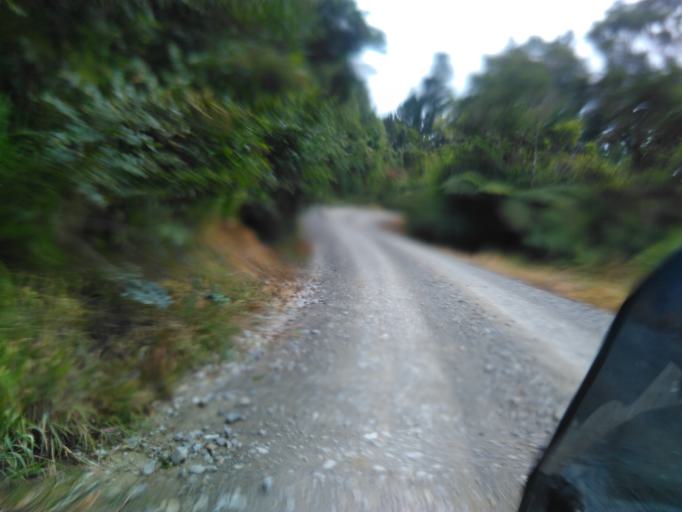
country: NZ
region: Gisborne
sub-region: Gisborne District
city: Gisborne
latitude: -38.1684
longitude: 178.1350
